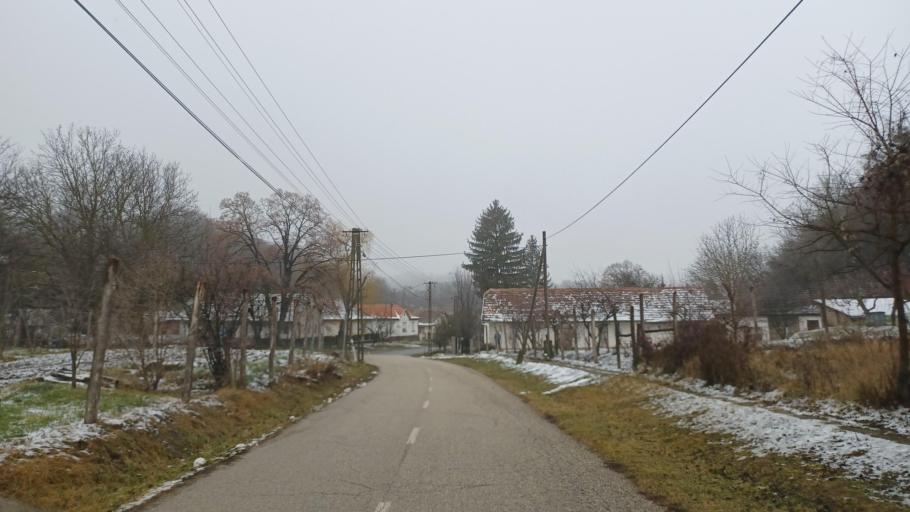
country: HU
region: Tolna
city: Pincehely
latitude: 46.6290
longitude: 18.4782
